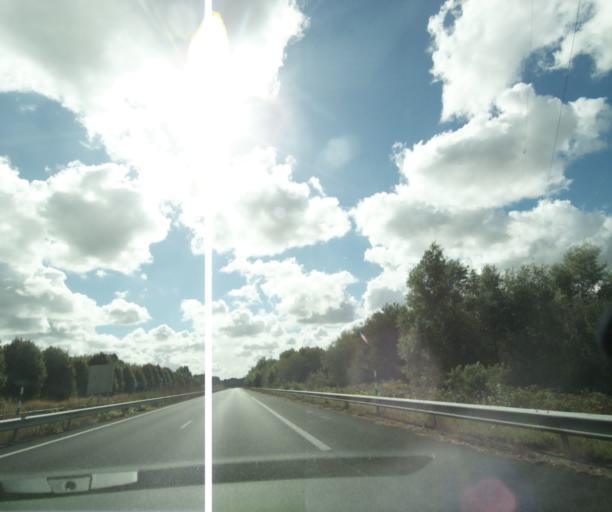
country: FR
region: Poitou-Charentes
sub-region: Departement de la Charente-Maritime
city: Cabariot
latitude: 45.9415
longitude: -0.8470
